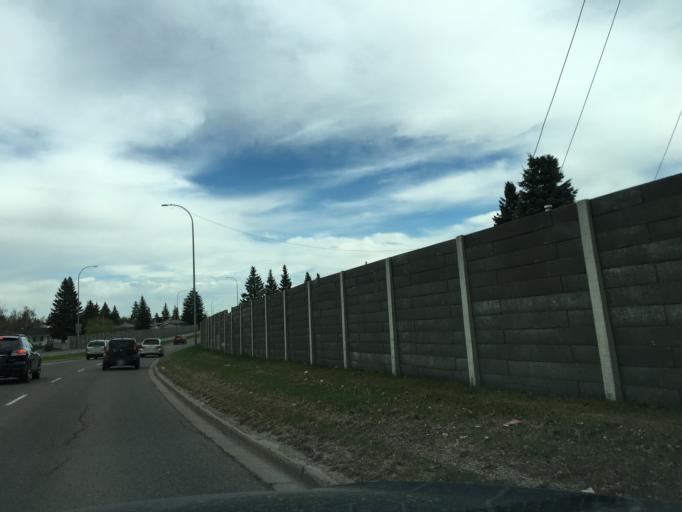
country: CA
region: Alberta
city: Calgary
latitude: 50.9649
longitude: -114.0656
